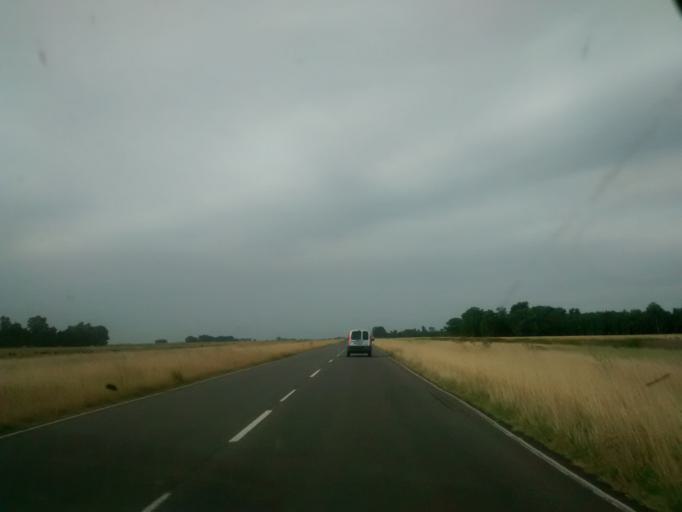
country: AR
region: Buenos Aires
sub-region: Partido de Rauch
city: Rauch
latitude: -36.5850
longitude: -58.5659
